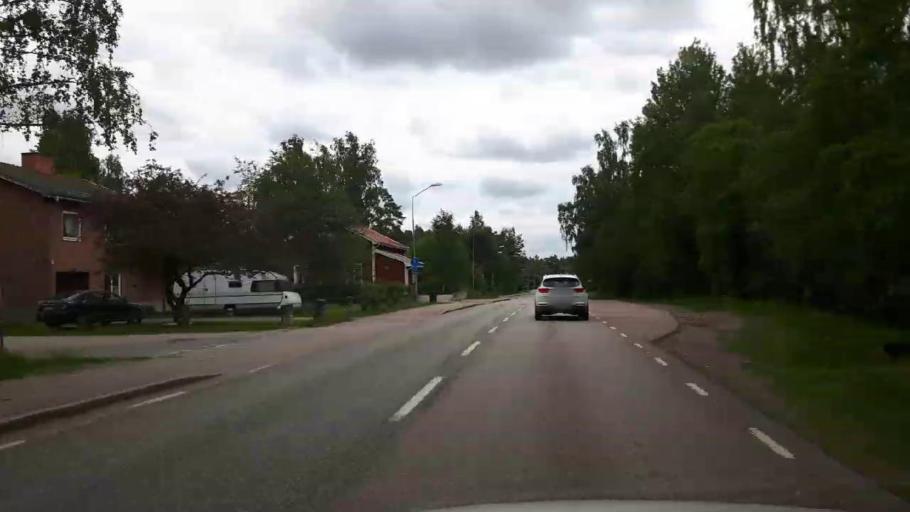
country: SE
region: Vaestmanland
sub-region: Norbergs Kommun
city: Norberg
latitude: 60.0978
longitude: 15.9307
